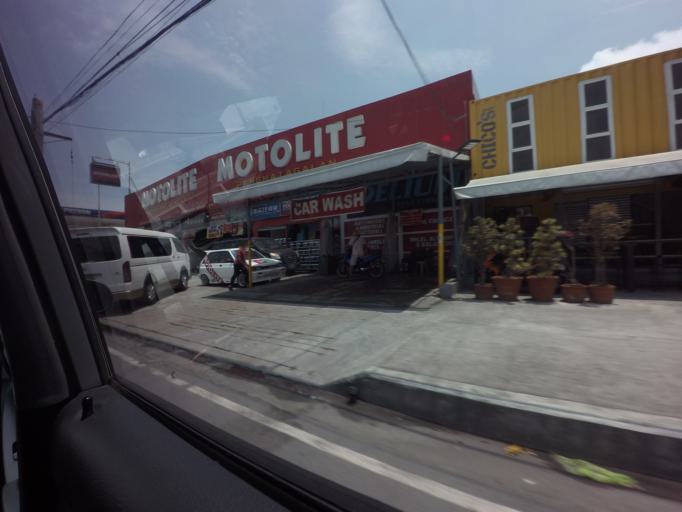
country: PH
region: Metro Manila
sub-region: City of Manila
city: Quiapo
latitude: 14.5922
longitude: 121.0015
